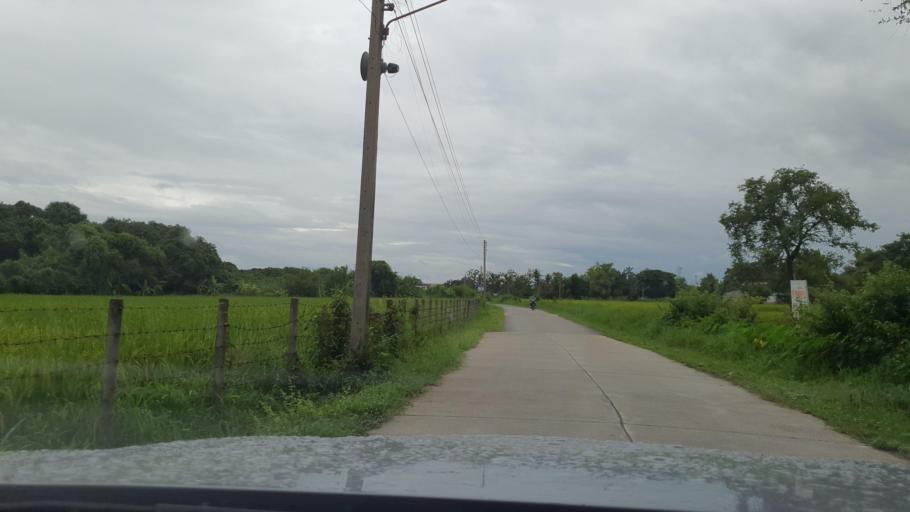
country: TH
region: Chiang Mai
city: Hang Dong
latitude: 18.6674
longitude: 98.9020
